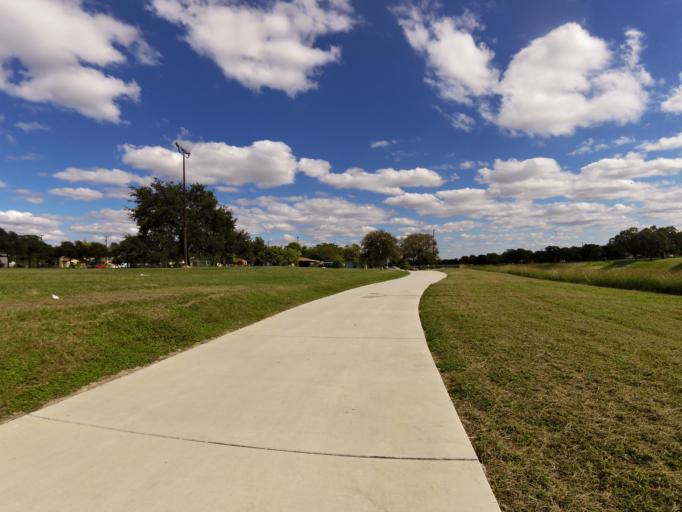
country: US
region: Texas
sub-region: Bexar County
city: San Antonio
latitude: 29.4139
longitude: -98.5230
